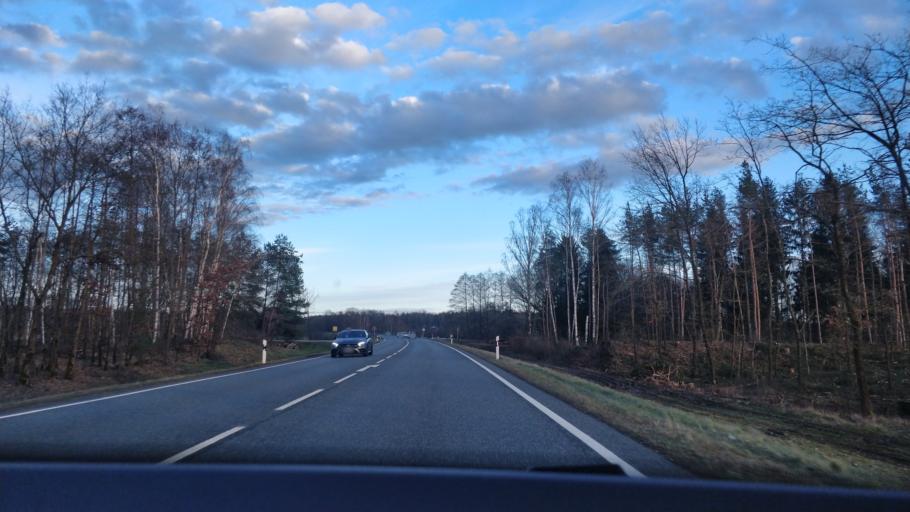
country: DE
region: Bavaria
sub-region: Upper Palatinate
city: Schwarzenbach
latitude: 49.7213
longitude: 11.9773
